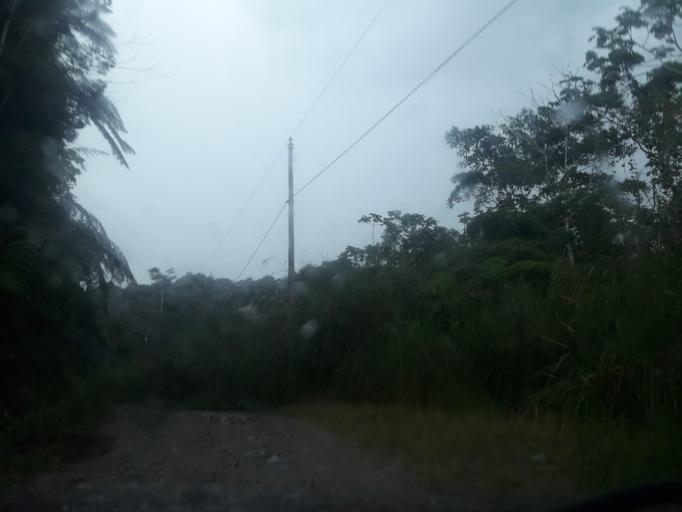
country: EC
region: Napo
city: Tena
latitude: -1.0990
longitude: -77.6924
